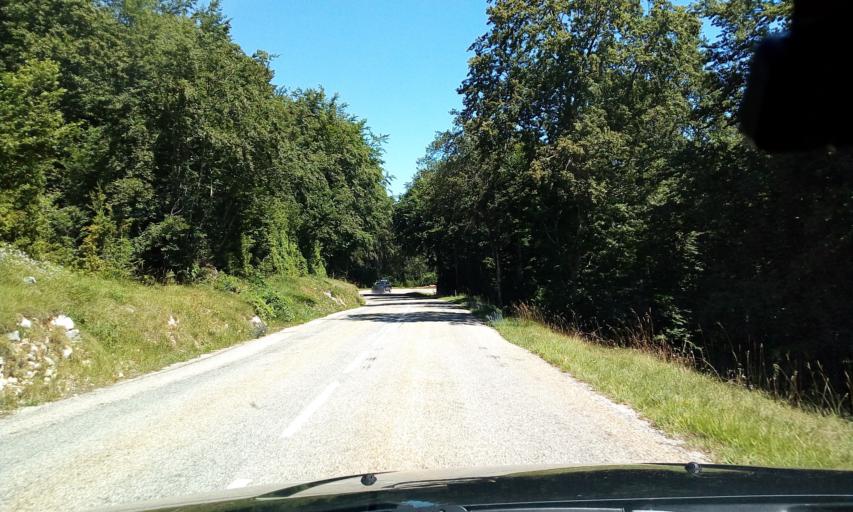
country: FR
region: Rhone-Alpes
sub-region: Departement de la Drome
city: Saint-Laurent-en-Royans
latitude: 44.9449
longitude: 5.3900
